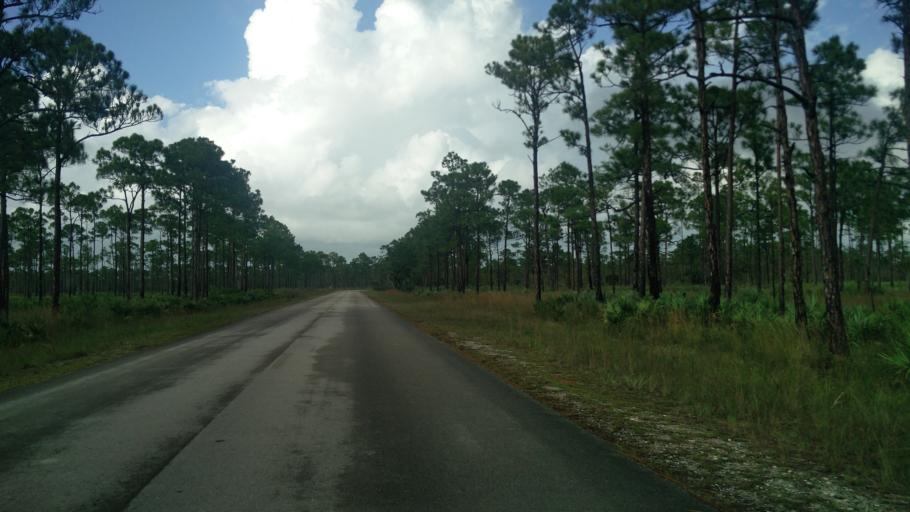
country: US
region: Florida
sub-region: Palm Beach County
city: Tequesta
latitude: 26.9983
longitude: -80.1461
